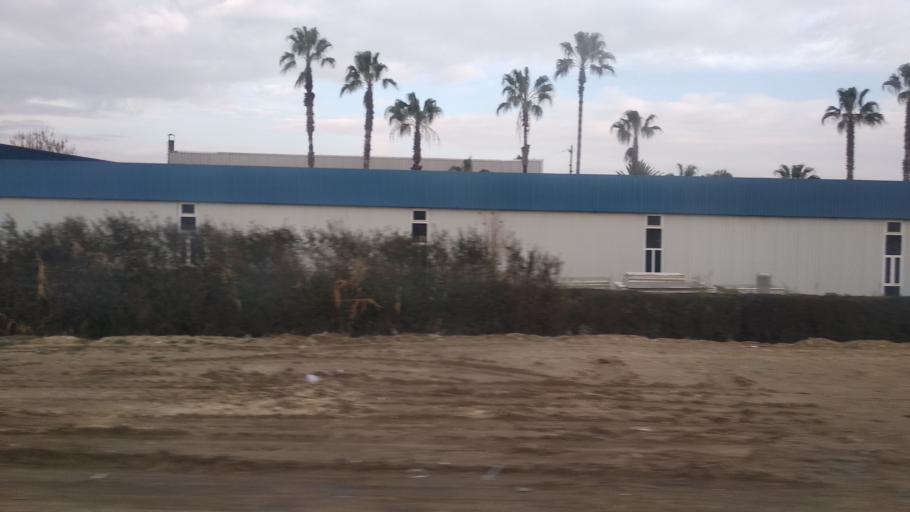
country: TR
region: Adana
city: Seyhan
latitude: 36.9952
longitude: 35.2179
